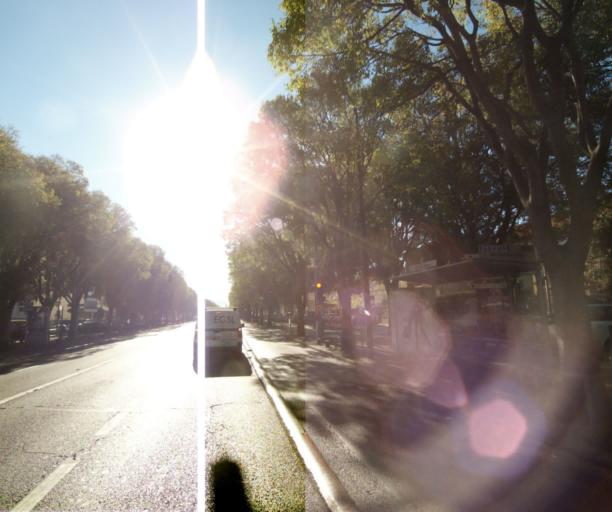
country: FR
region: Provence-Alpes-Cote d'Azur
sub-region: Departement des Bouches-du-Rhone
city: Marseille 09
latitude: 43.2649
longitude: 5.3956
